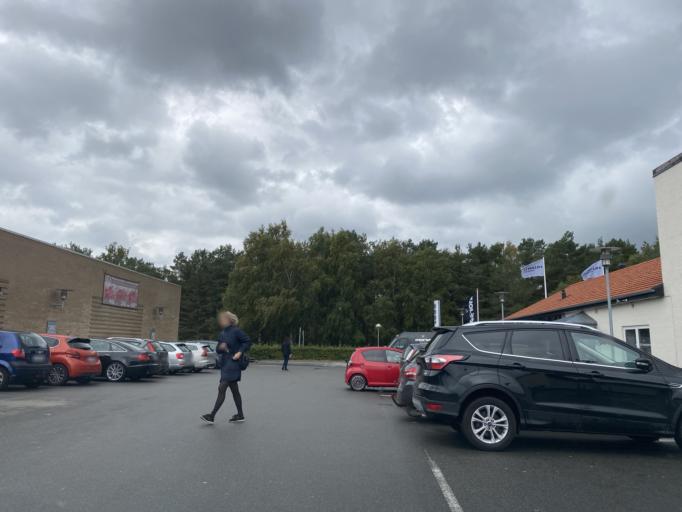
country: DK
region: Central Jutland
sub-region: Silkeborg Kommune
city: Svejbaek
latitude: 56.1762
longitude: 9.6269
